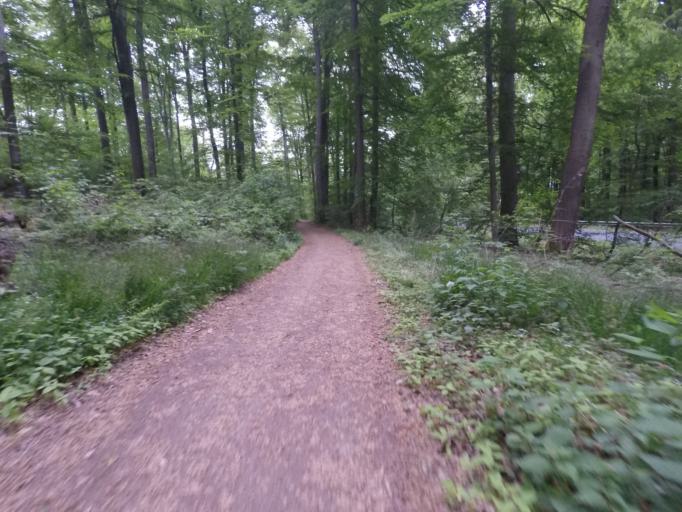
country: DE
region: North Rhine-Westphalia
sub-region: Regierungsbezirk Detmold
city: Bad Salzuflen
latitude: 52.1079
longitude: 8.7571
